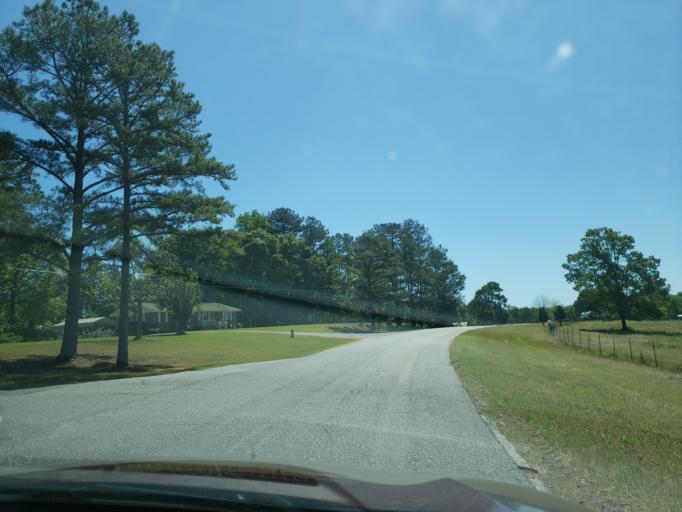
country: US
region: Alabama
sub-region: Tallapoosa County
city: Dadeville
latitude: 32.6992
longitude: -85.8597
